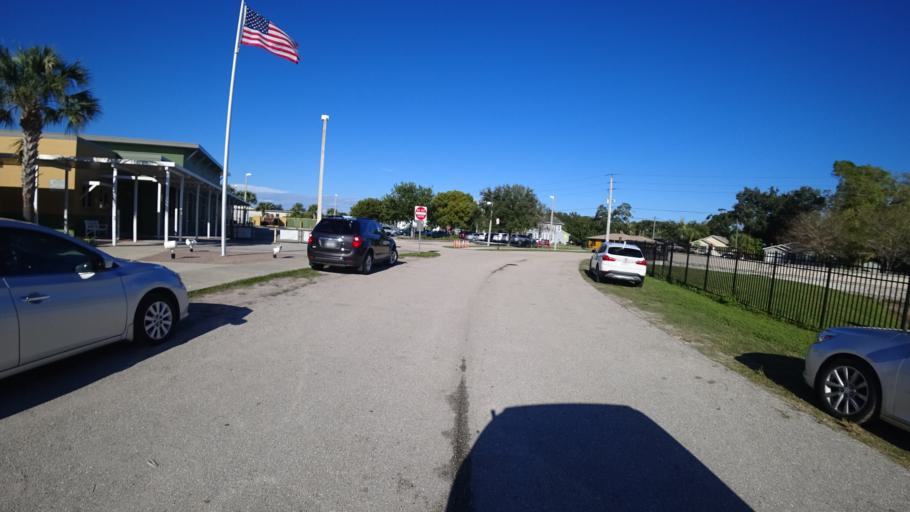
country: US
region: Florida
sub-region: Manatee County
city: Bradenton
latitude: 27.4875
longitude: -82.5673
